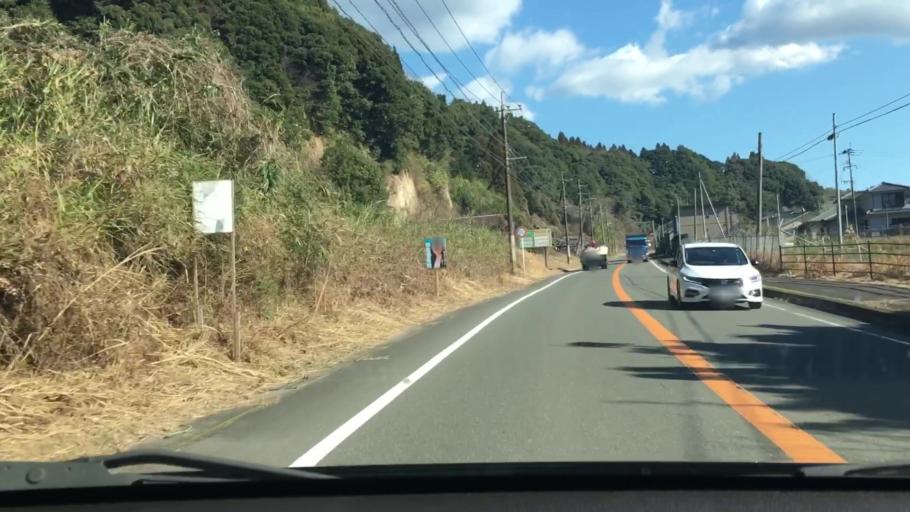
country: JP
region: Kagoshima
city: Satsumasendai
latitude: 31.7990
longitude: 130.4151
